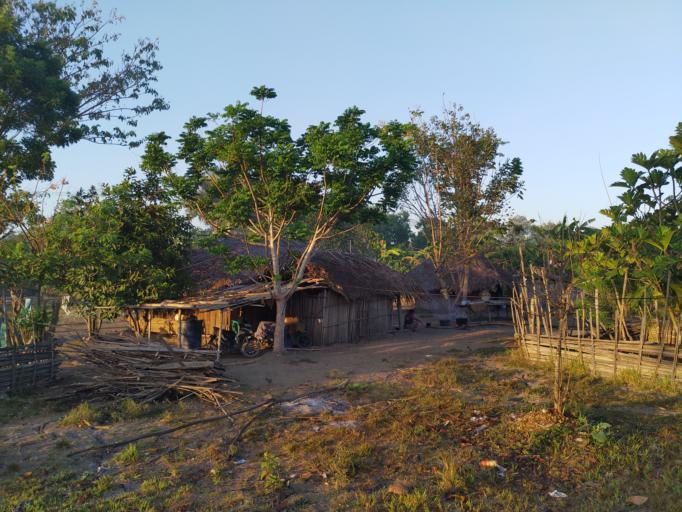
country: TL
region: Viqueque
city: Viqueque
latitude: -8.9335
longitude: 126.1660
